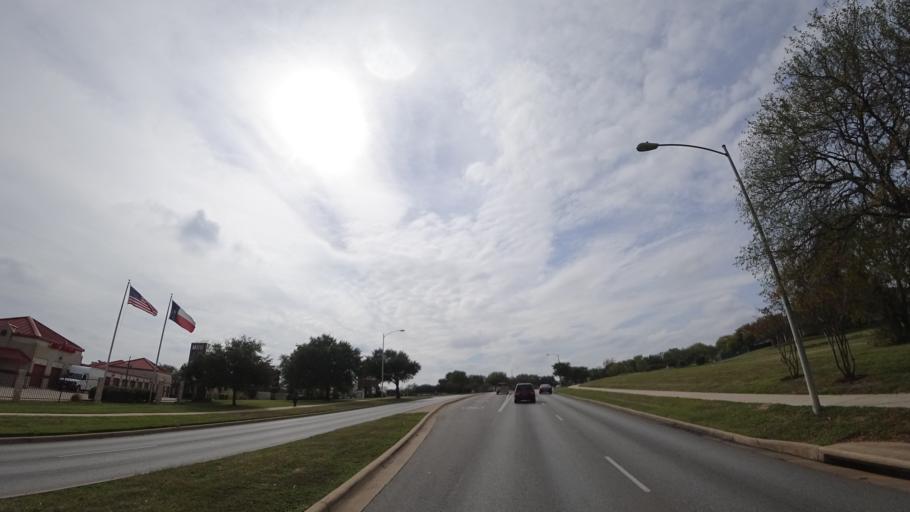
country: US
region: Texas
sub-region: Travis County
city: Wells Branch
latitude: 30.4371
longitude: -97.6737
